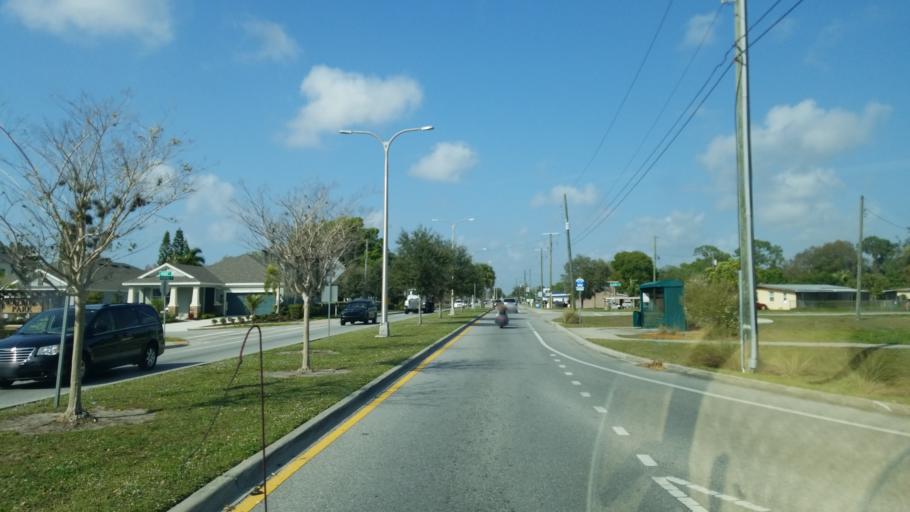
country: US
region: Florida
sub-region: Sarasota County
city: Fruitville
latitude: 27.3269
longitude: -82.4638
